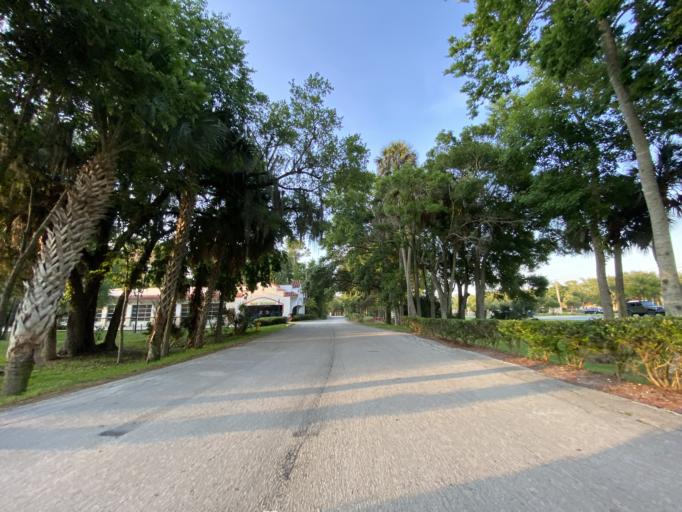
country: US
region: Florida
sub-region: Volusia County
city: Port Orange
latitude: 29.1298
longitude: -81.0033
